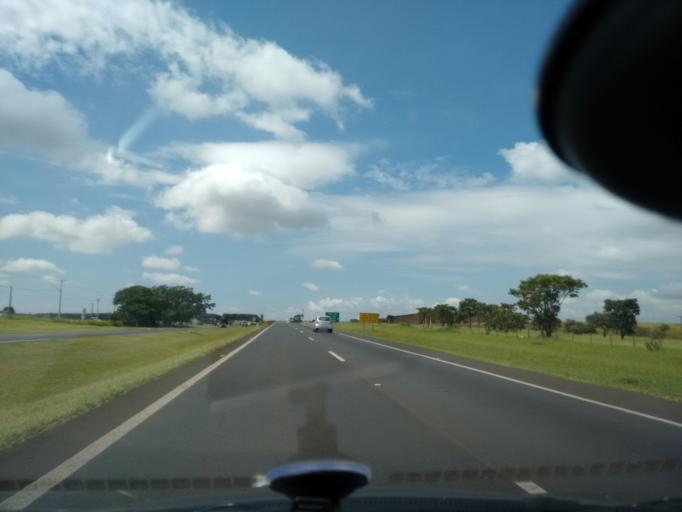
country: BR
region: Sao Paulo
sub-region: Ibate
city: Ibate
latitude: -21.9388
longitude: -48.0093
